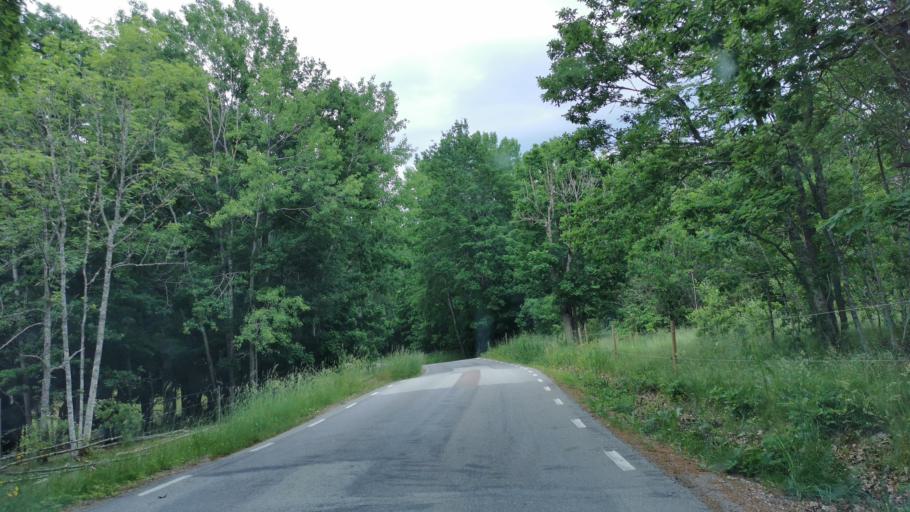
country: SE
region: Vaestra Goetaland
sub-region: Bengtsfors Kommun
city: Dals Langed
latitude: 58.8444
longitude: 12.4089
